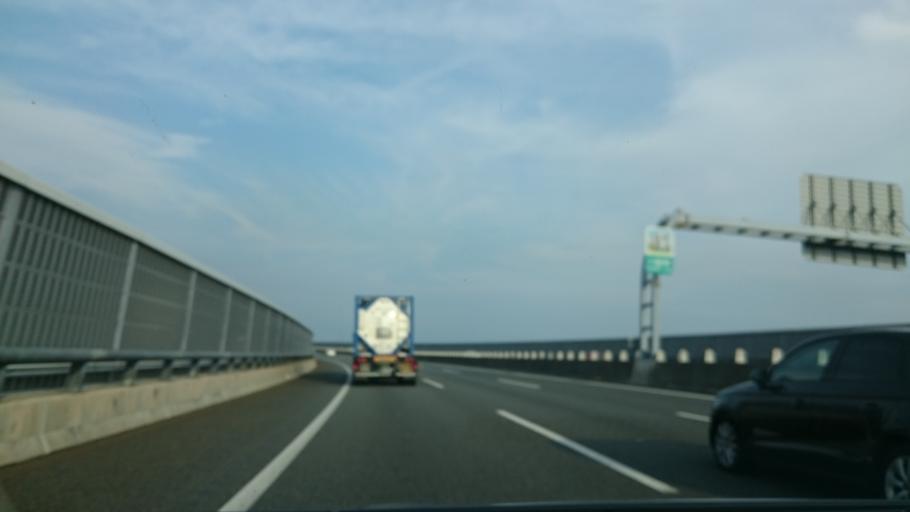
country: JP
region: Mie
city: Yokkaichi
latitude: 35.0276
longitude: 136.6483
